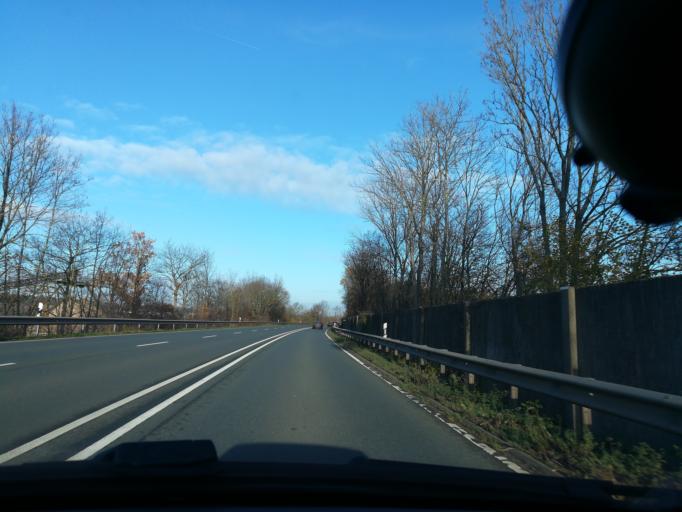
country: DE
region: North Rhine-Westphalia
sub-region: Regierungsbezirk Detmold
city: Petershagen
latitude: 52.3460
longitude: 8.9618
